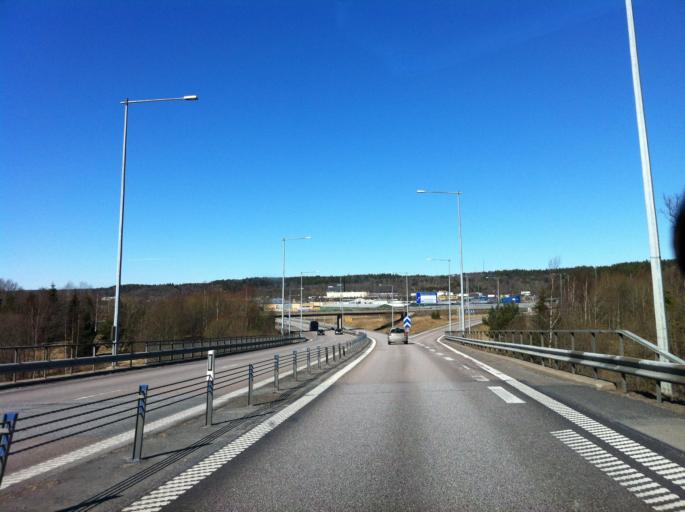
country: SE
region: Vaestra Goetaland
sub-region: Vanersborgs Kommun
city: Vanersborg
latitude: 58.3682
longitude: 12.3228
